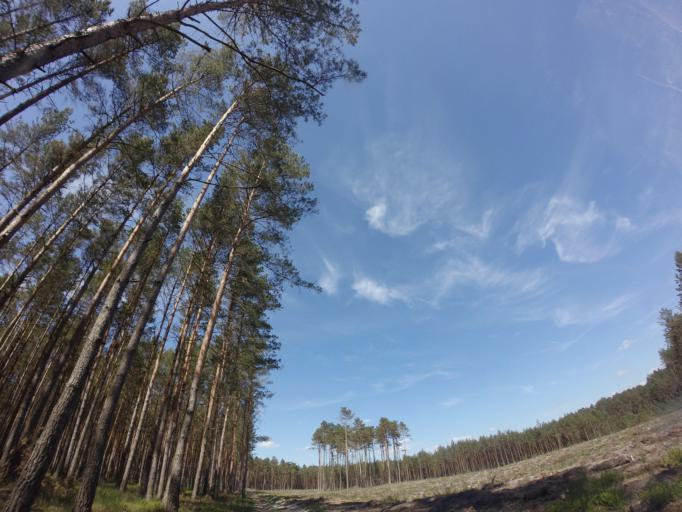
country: PL
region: West Pomeranian Voivodeship
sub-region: Powiat choszczenski
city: Drawno
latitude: 53.1343
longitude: 15.7896
